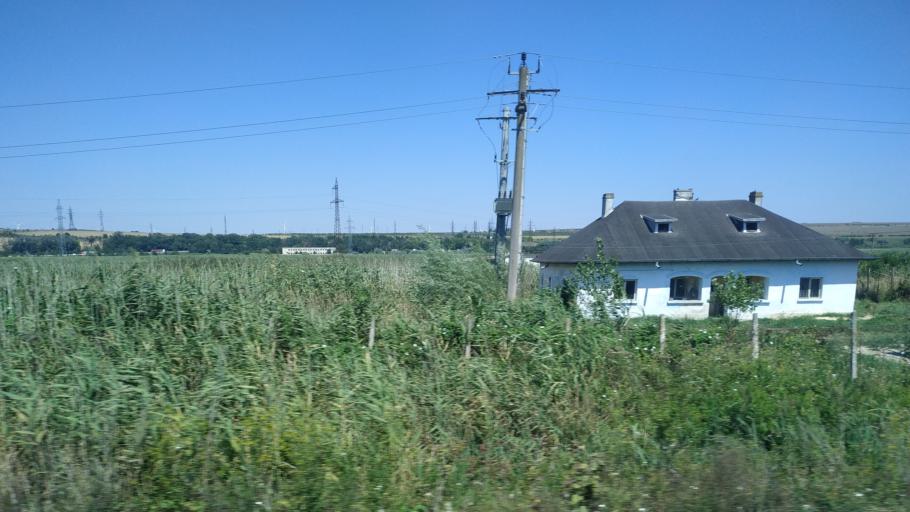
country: RO
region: Constanta
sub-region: Comuna Mircea Voda
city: Satu Nou
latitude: 44.2620
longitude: 28.1961
